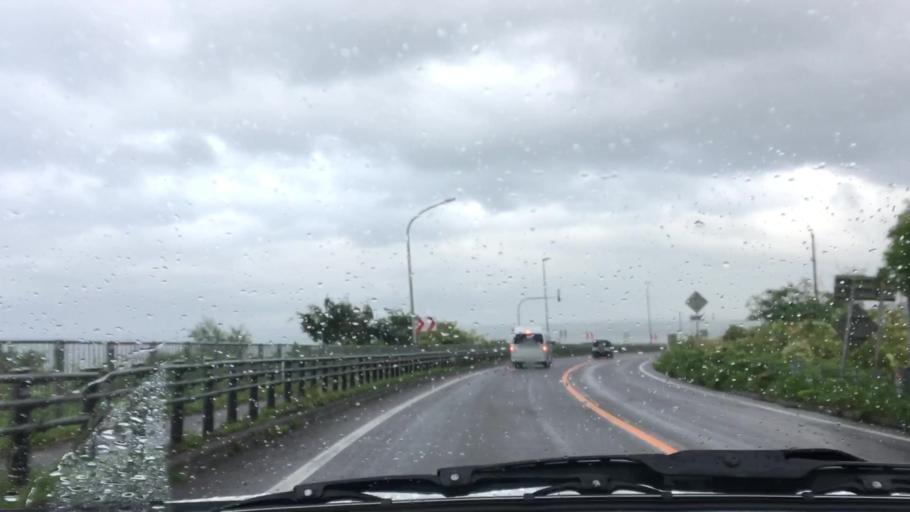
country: JP
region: Hokkaido
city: Nanae
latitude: 42.2343
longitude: 140.3202
